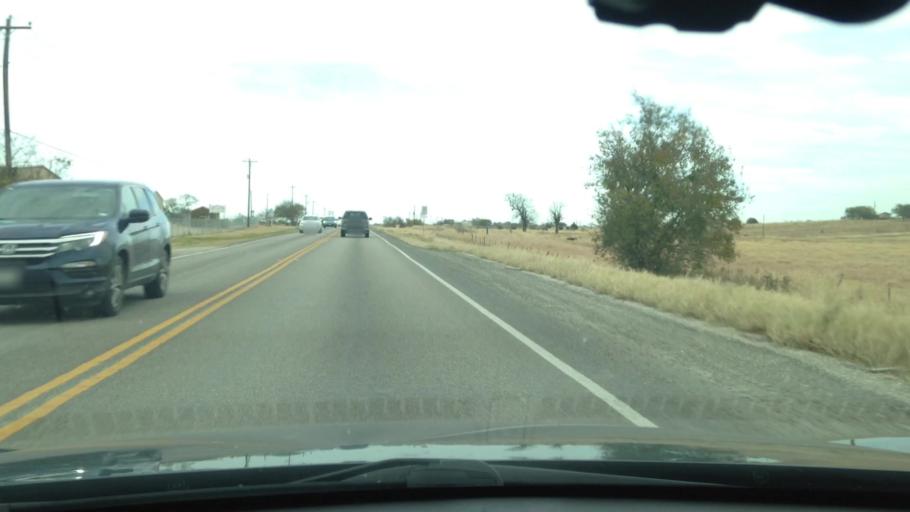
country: US
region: Texas
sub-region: Caldwell County
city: Martindale
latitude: 29.9118
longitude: -97.8555
